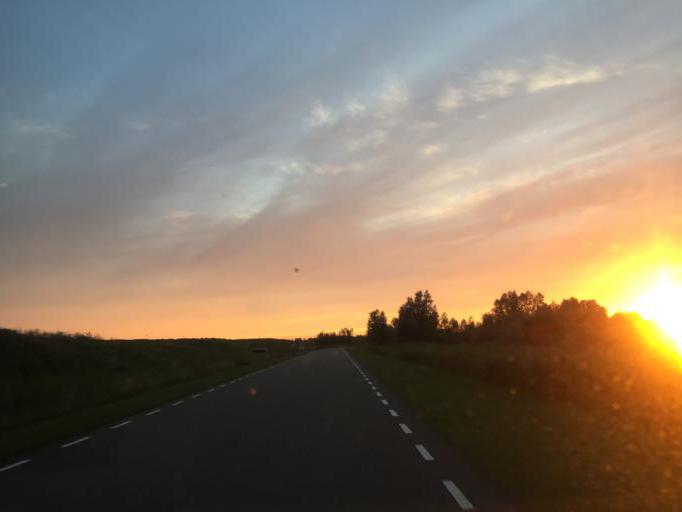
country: NL
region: Friesland
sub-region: Gemeente Dongeradeel
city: Anjum
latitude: 53.3752
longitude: 6.1564
